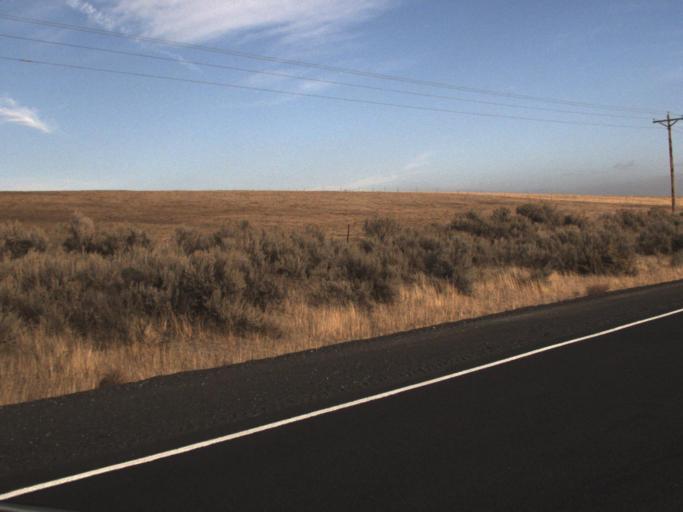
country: US
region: Washington
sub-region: Grant County
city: Warden
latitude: 47.3354
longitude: -118.8934
